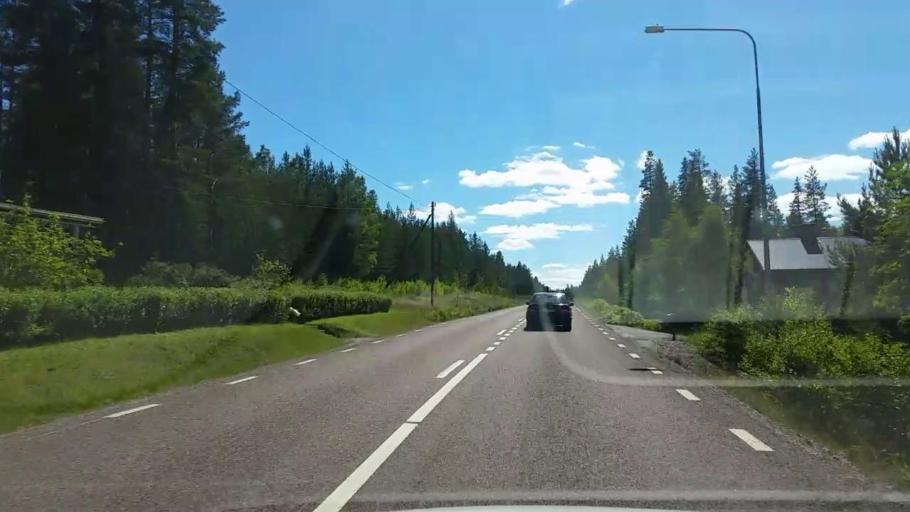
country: SE
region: Gaevleborg
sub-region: Ovanakers Kommun
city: Edsbyn
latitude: 61.2688
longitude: 15.8922
